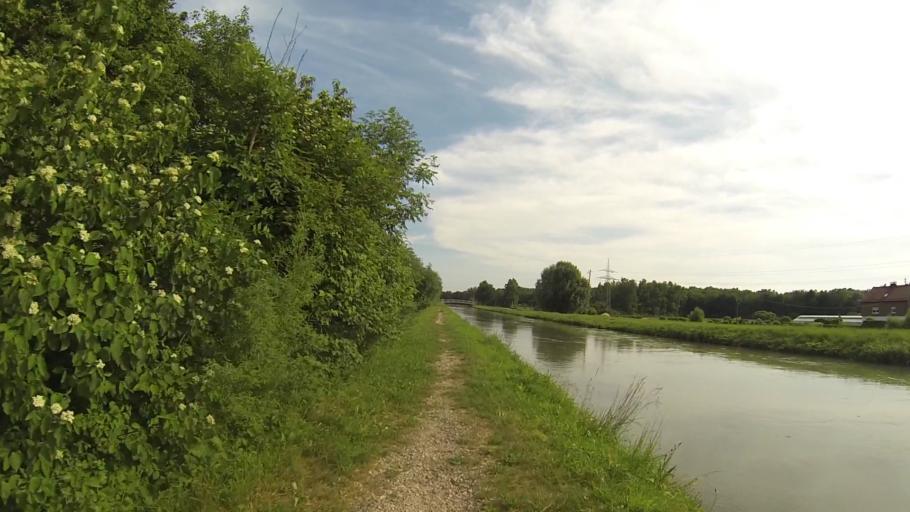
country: DE
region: Bavaria
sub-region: Swabia
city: Neu-Ulm
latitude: 48.3668
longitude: 10.0044
